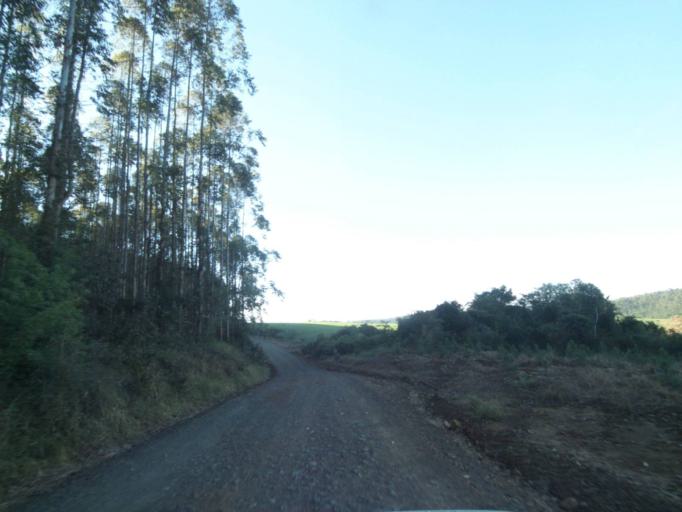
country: BR
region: Parana
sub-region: Telemaco Borba
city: Telemaco Borba
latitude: -24.4433
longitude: -50.6000
